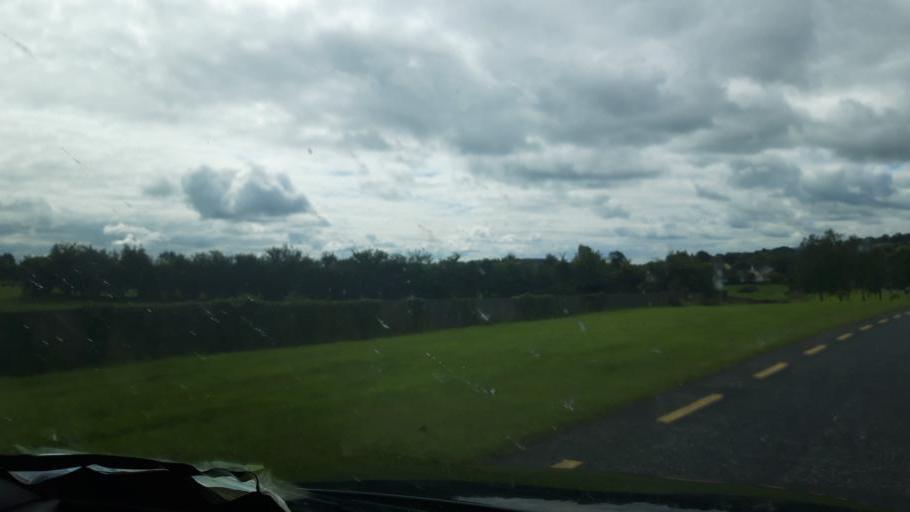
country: IE
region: Munster
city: Carrick-on-Suir
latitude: 52.4496
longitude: -7.4688
